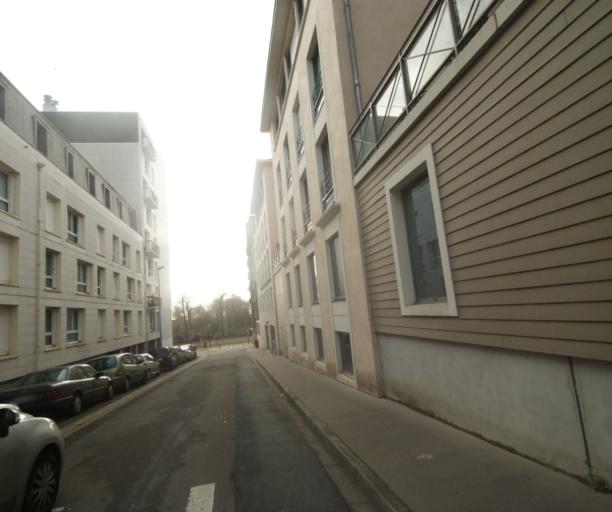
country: FR
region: Pays de la Loire
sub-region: Departement de la Sarthe
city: Le Mans
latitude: 48.0113
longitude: 0.2027
